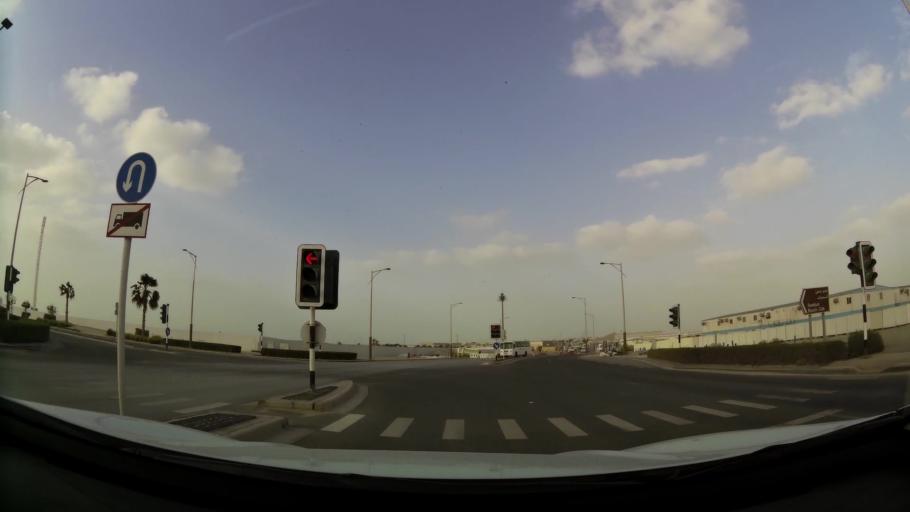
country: AE
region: Abu Dhabi
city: Abu Dhabi
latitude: 24.5600
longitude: 54.4563
